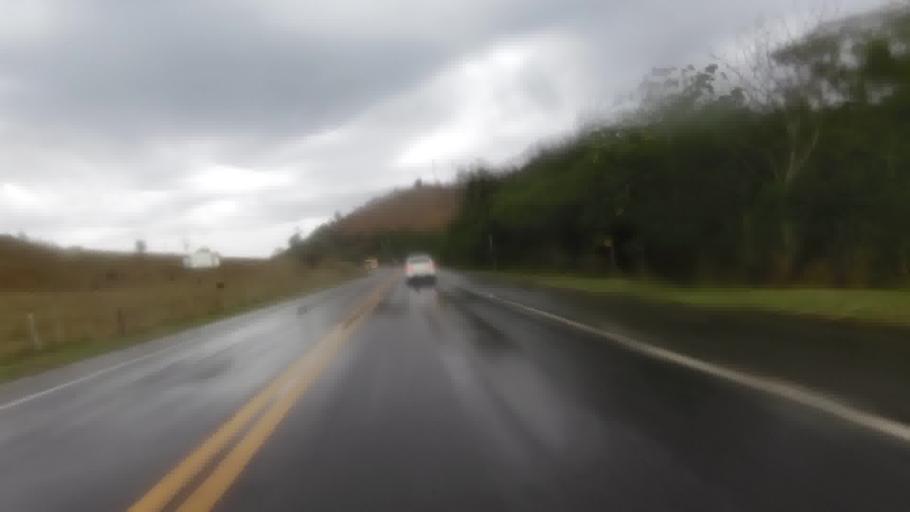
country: BR
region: Espirito Santo
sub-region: Cachoeiro De Itapemirim
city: Cachoeiro de Itapemirim
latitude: -20.9645
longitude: -41.1061
